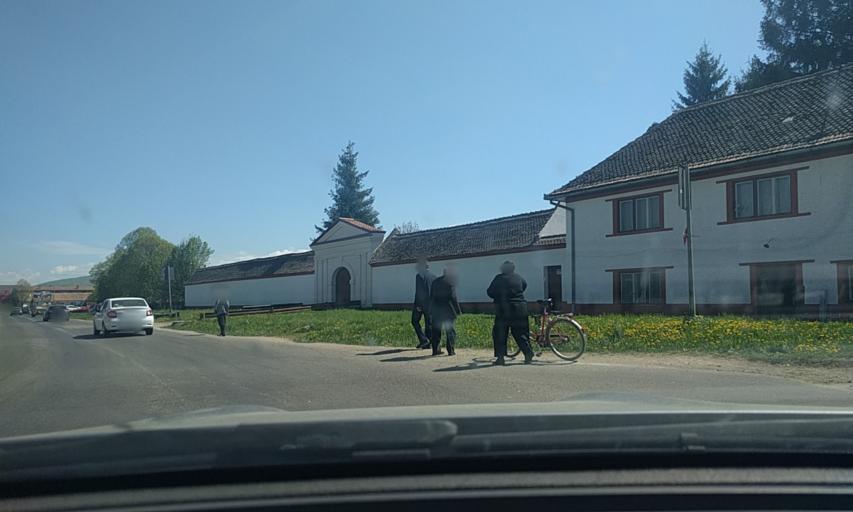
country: RO
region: Brasov
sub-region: Comuna Prejmer
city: Prejmer
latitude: 45.7145
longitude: 25.7783
